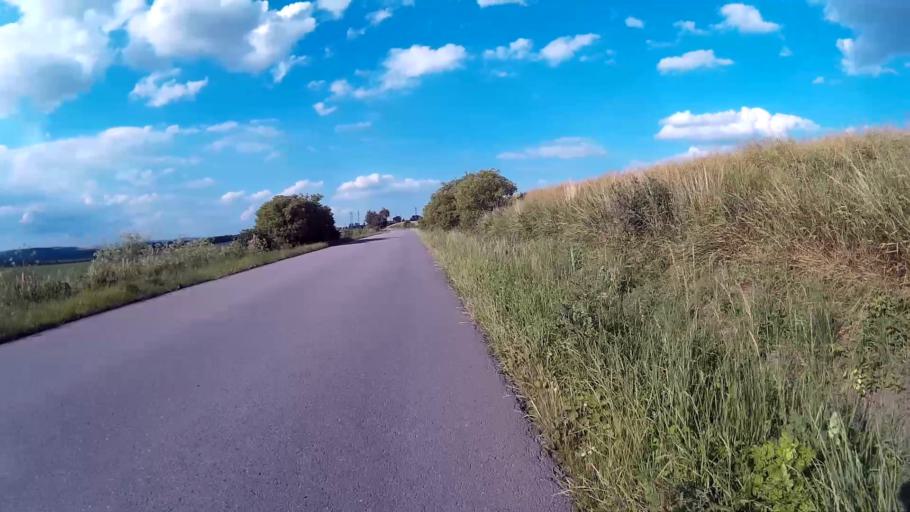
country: CZ
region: South Moravian
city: Tesany
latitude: 49.0622
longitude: 16.7847
